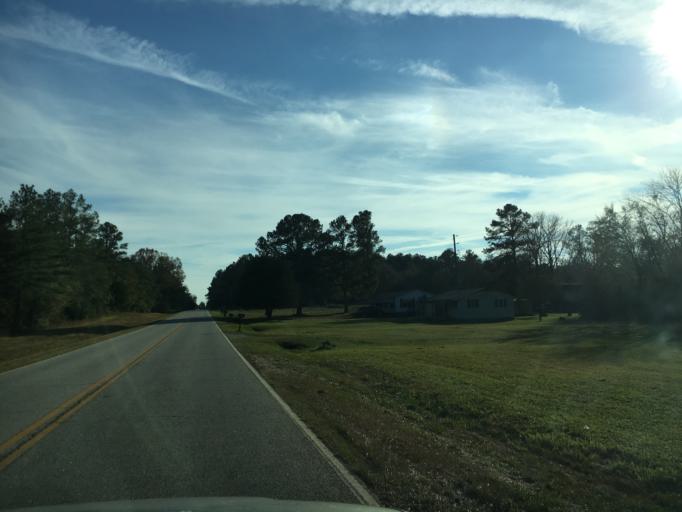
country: US
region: Georgia
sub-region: Elbert County
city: Elberton
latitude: 34.0095
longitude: -82.7804
